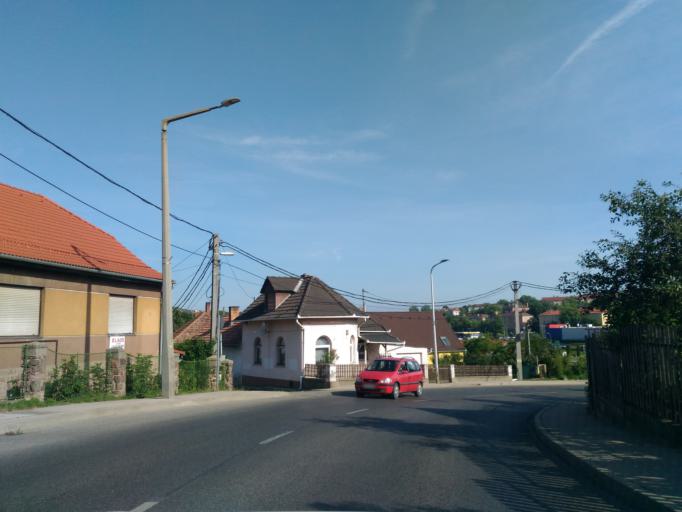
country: HU
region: Baranya
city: Komlo
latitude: 46.1889
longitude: 18.2593
